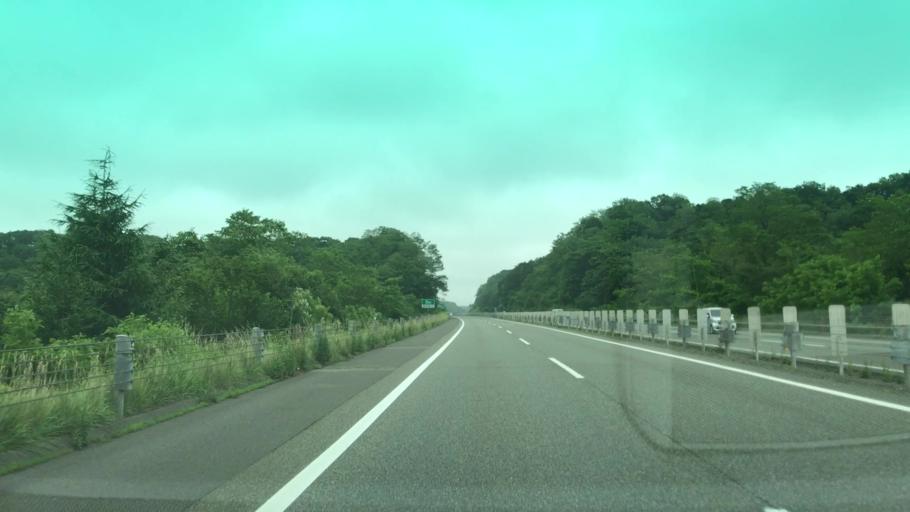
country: JP
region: Hokkaido
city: Tomakomai
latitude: 42.6431
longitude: 141.5247
